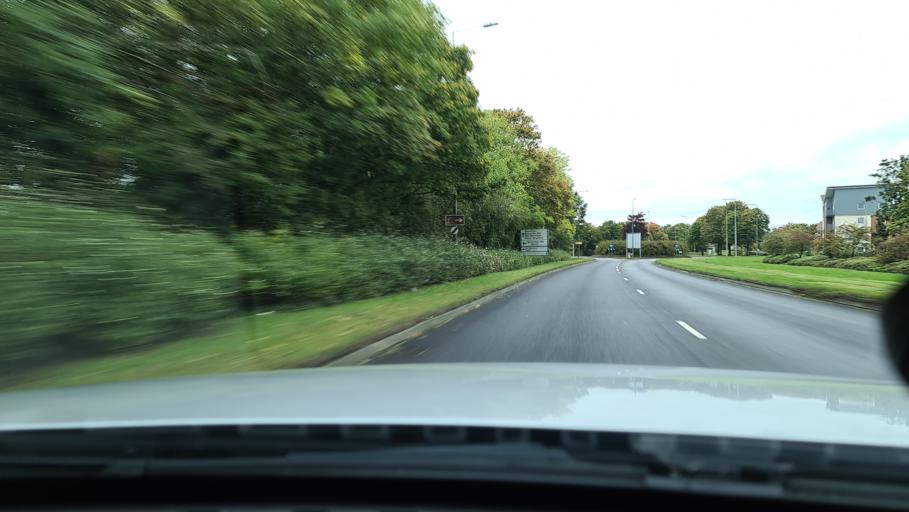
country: GB
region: England
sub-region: Milton Keynes
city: Stony Stratford
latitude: 52.0571
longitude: -0.8247
